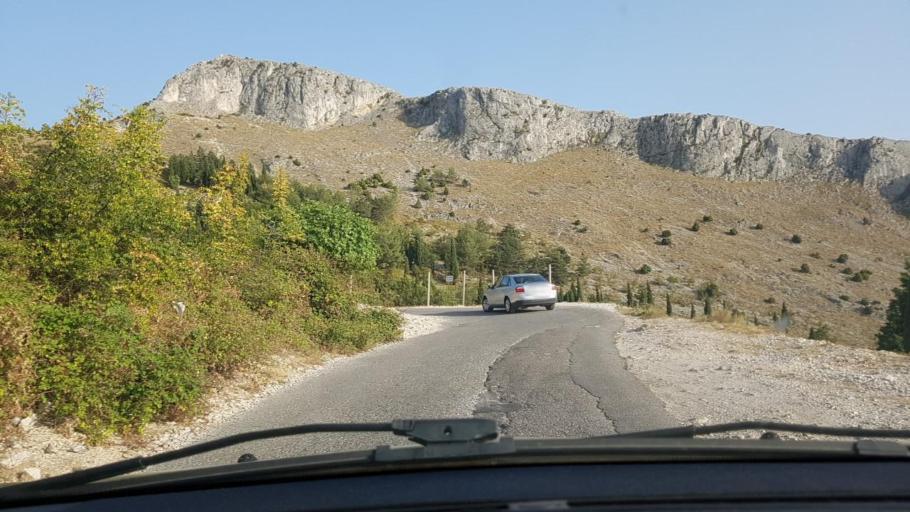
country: BA
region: Federation of Bosnia and Herzegovina
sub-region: Hercegovacko-Bosanski Kanton
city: Mostar
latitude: 43.3473
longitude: 17.8263
